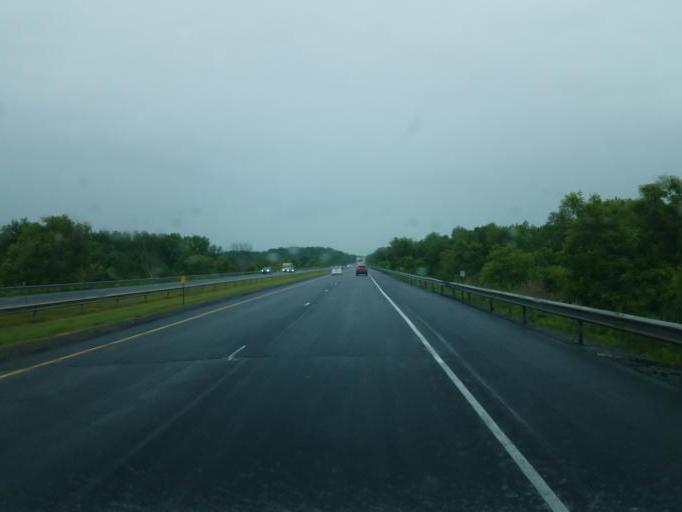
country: US
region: New York
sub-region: Oneida County
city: Whitesboro
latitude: 43.1339
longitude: -75.2892
